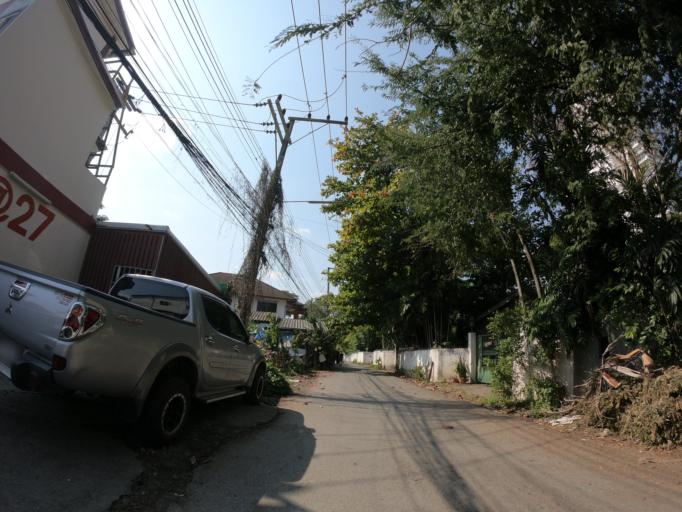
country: TH
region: Chiang Mai
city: Chiang Mai
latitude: 18.7909
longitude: 99.0063
